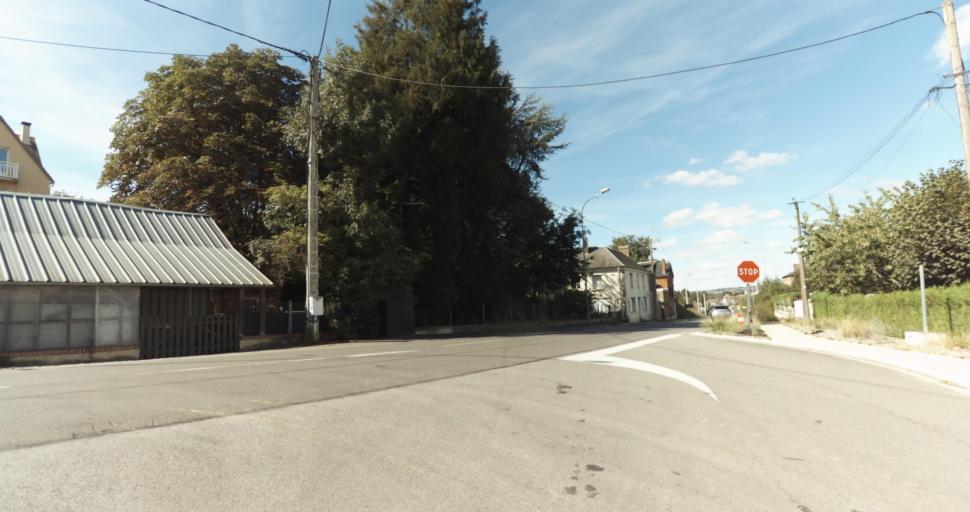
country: FR
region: Lower Normandy
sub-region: Departement de l'Orne
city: Vimoutiers
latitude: 48.9204
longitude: 0.1997
